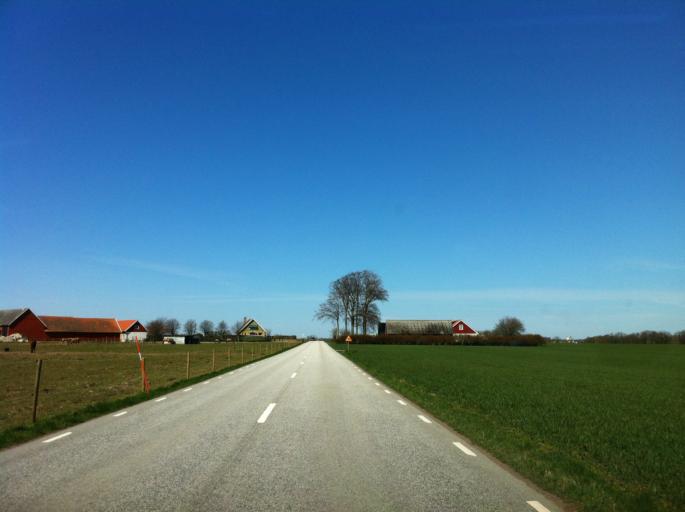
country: SE
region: Skane
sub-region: Helsingborg
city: Glumslov
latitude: 55.9712
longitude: 12.8224
